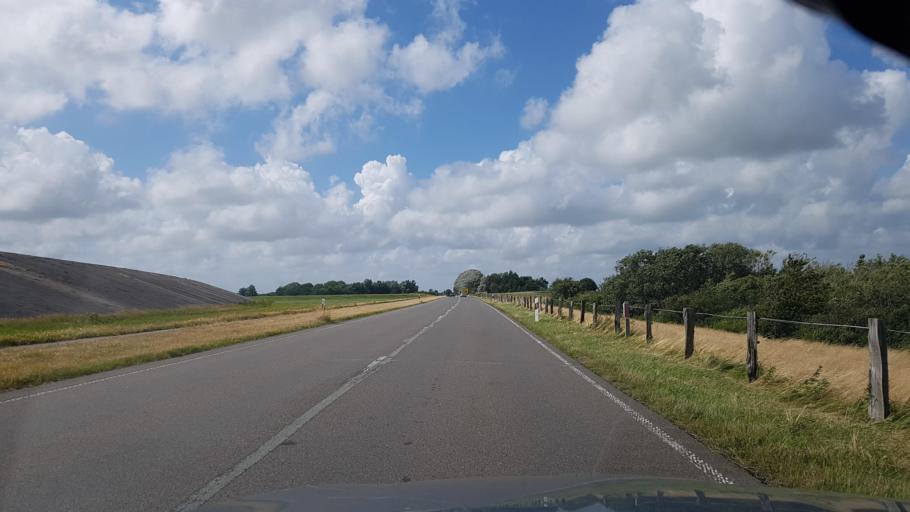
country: DE
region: Schleswig-Holstein
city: Vollerwiek
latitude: 54.2908
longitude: 8.8309
